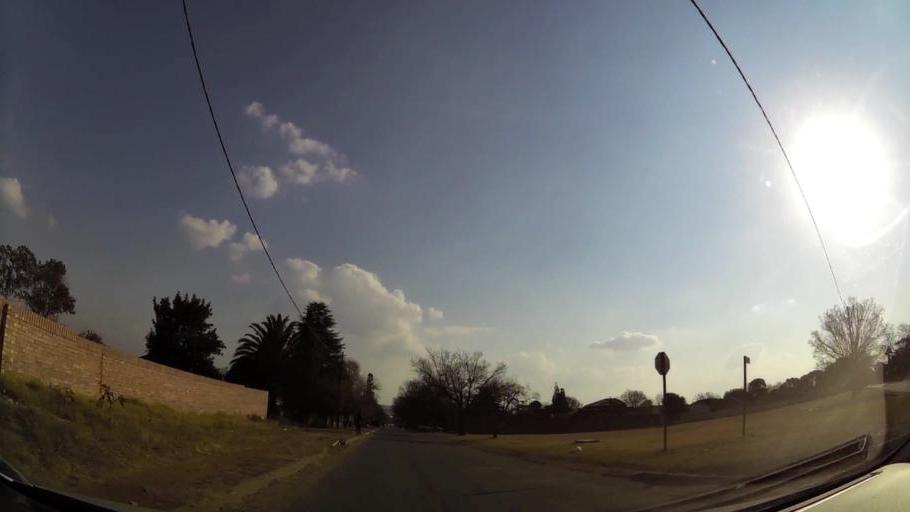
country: ZA
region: Gauteng
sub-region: Ekurhuleni Metropolitan Municipality
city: Tembisa
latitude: -25.9572
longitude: 28.2257
